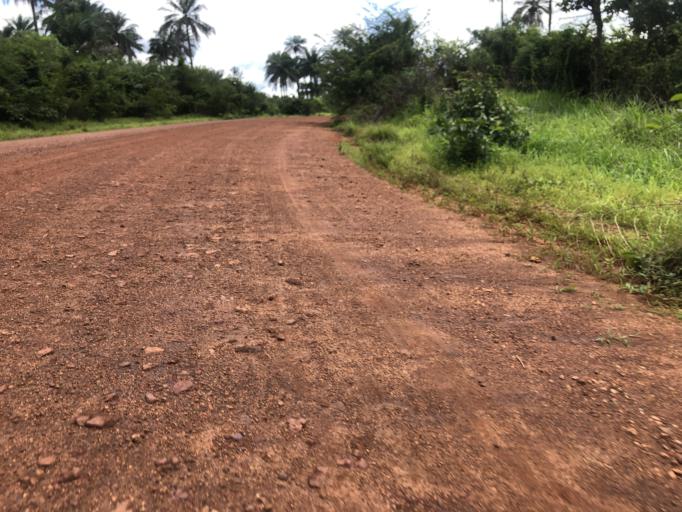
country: SL
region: Northern Province
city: Port Loko
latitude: 8.7150
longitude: -12.8352
